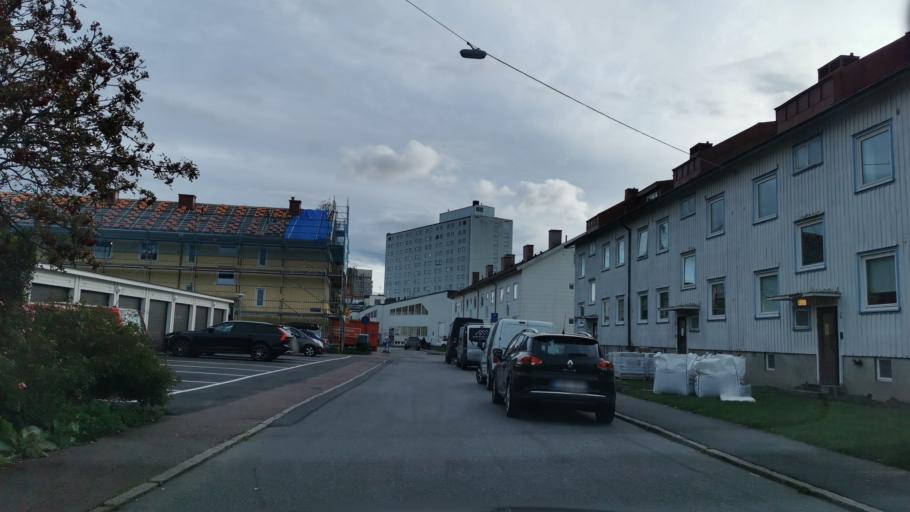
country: SE
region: Vaestra Goetaland
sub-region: Goteborg
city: Eriksbo
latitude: 57.7324
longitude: 12.0137
